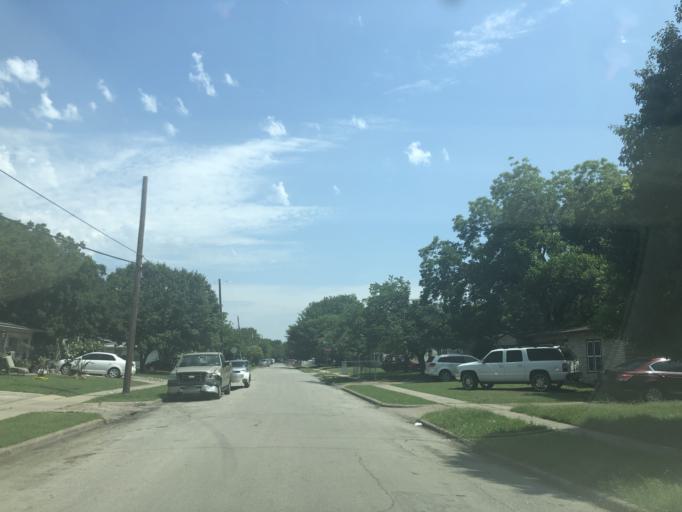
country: US
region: Texas
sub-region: Dallas County
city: Grand Prairie
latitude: 32.7325
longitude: -97.0140
